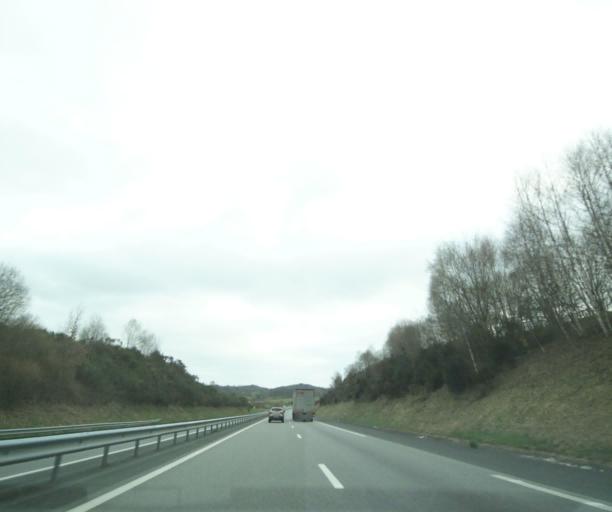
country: FR
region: Limousin
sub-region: Departement de la Correze
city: Vigeois
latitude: 45.3424
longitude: 1.5716
